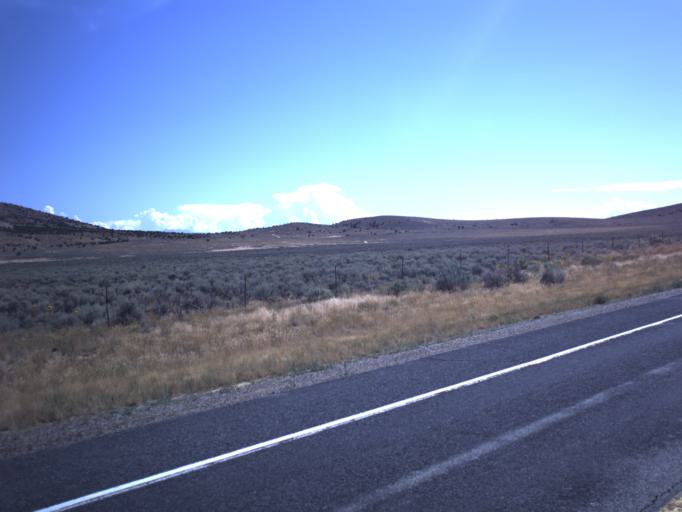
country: US
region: Utah
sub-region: Utah County
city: Eagle Mountain
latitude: 40.0781
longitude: -112.3957
